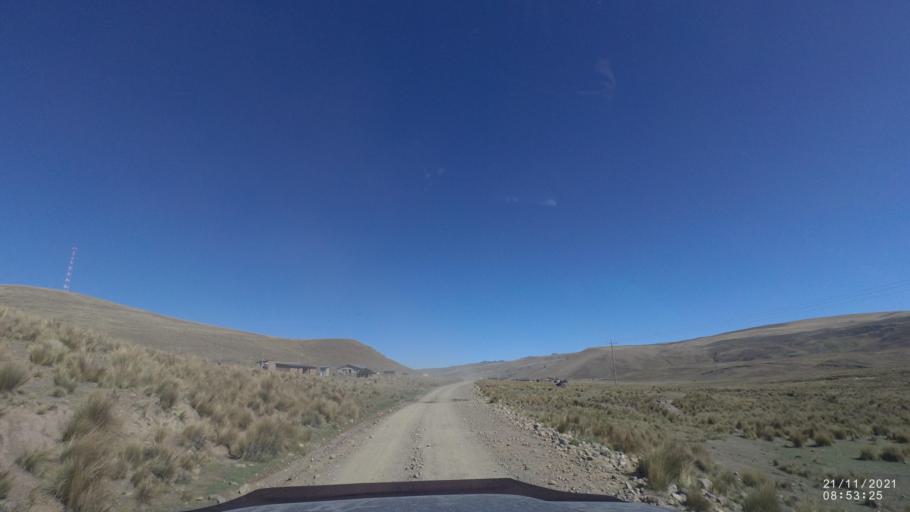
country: BO
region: Cochabamba
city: Cochabamba
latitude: -17.2084
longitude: -66.2414
